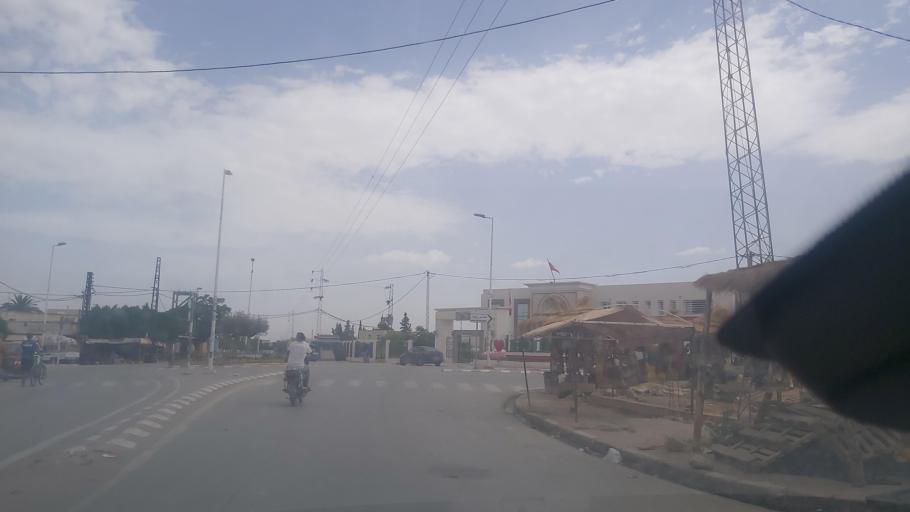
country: TN
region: Silyanah
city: Bu `Aradah
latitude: 36.3510
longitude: 9.6236
